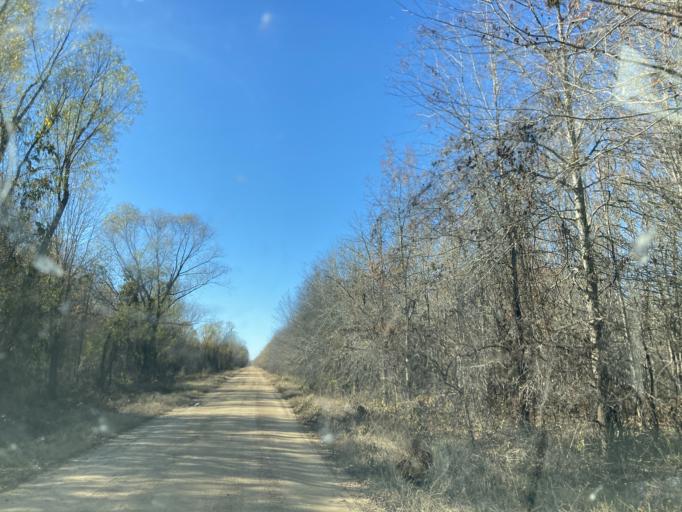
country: US
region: Mississippi
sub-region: Sharkey County
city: Rolling Fork
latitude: 32.7491
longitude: -90.6665
